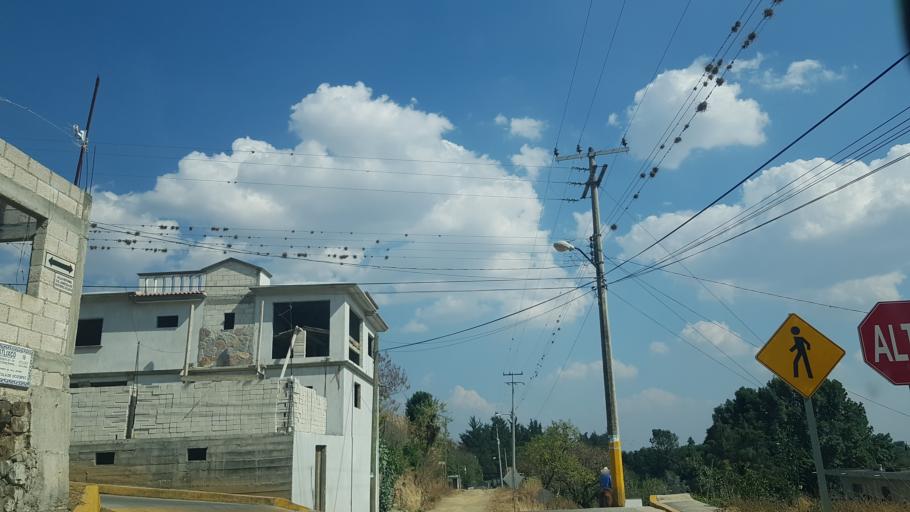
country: MX
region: Puebla
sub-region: Atlixco
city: Colonia Agricola de Ocotepec (Colonia San Jose)
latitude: 18.9258
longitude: -98.5421
